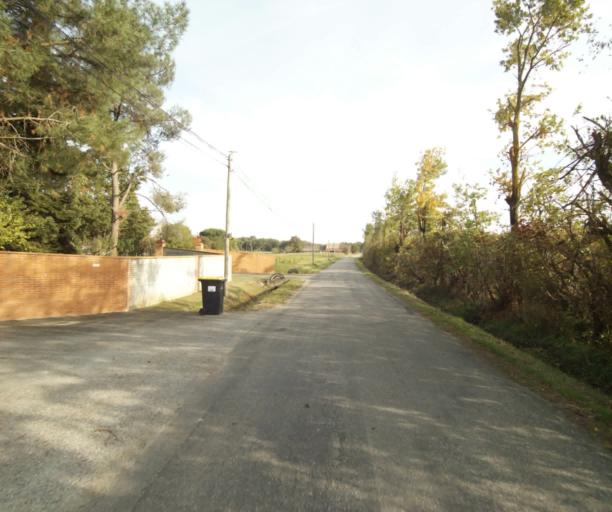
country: FR
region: Midi-Pyrenees
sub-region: Departement du Tarn-et-Garonne
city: Campsas
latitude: 43.8890
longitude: 1.3095
